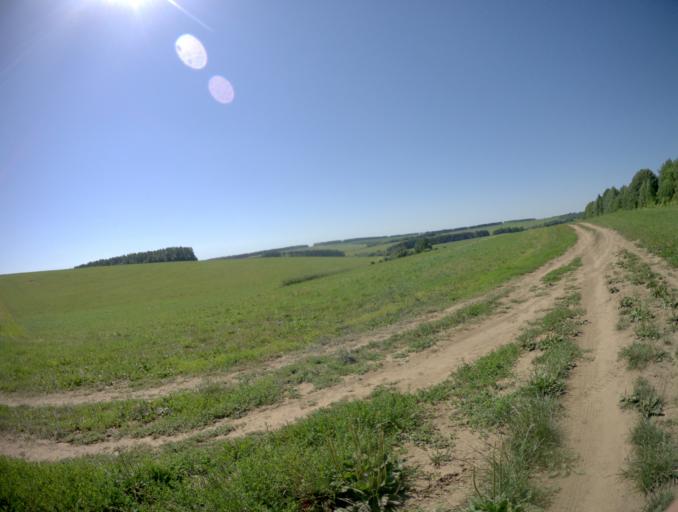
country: RU
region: Nizjnij Novgorod
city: Reshetikha
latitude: 56.1604
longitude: 43.3383
